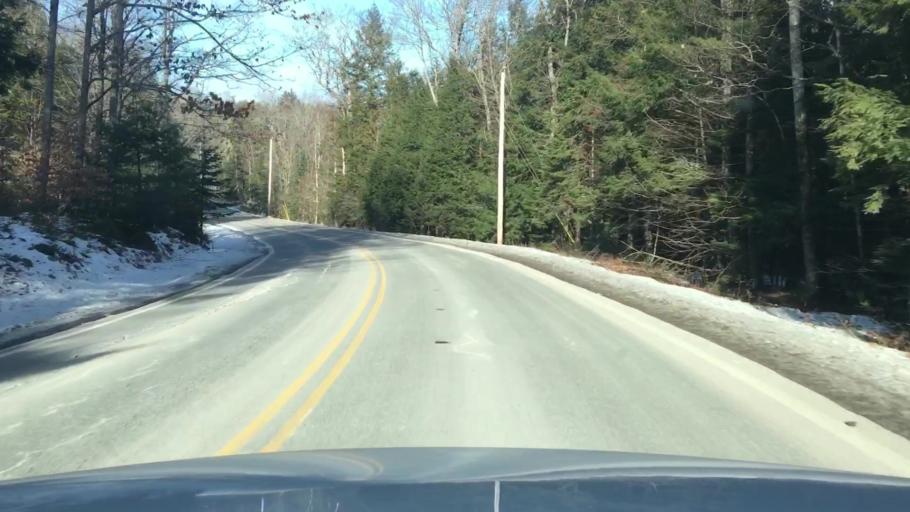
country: US
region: Maine
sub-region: Hancock County
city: Dedham
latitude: 44.6345
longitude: -68.6996
